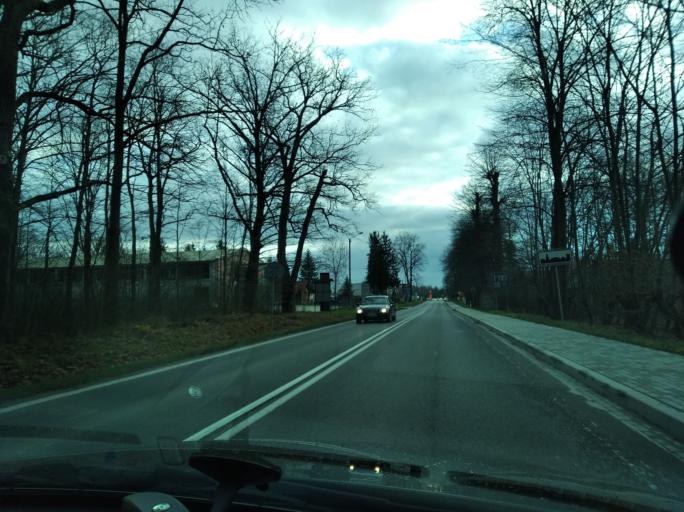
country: PL
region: Subcarpathian Voivodeship
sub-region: Powiat lancucki
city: Rakszawa
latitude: 50.1248
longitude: 22.2315
